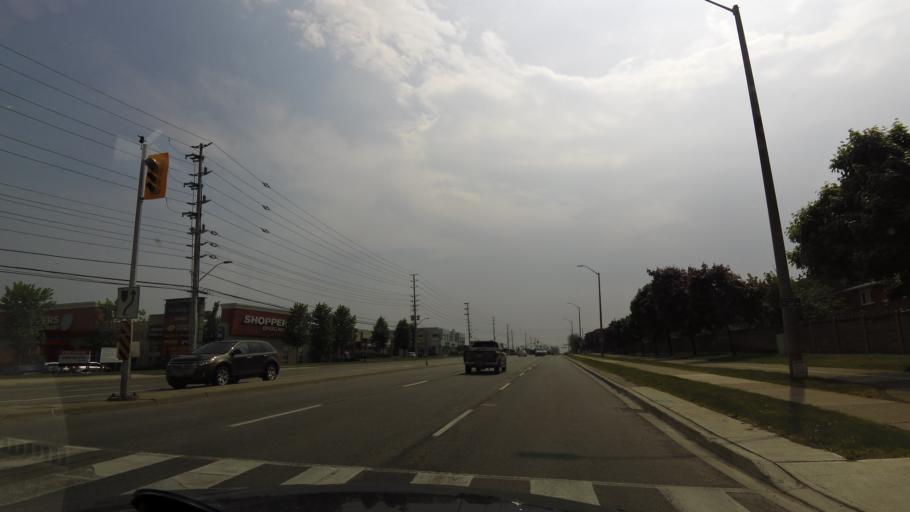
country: CA
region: Ontario
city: Mississauga
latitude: 43.5816
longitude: -79.6493
